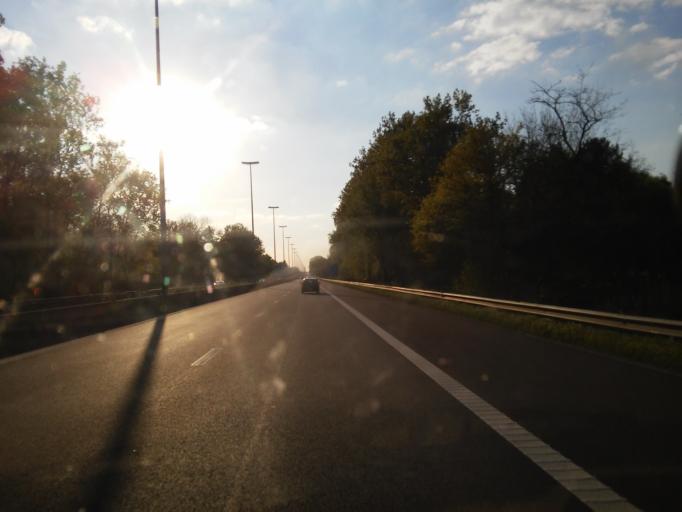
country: BE
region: Flanders
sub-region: Provincie Antwerpen
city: Meerhout
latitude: 51.1020
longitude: 5.0477
